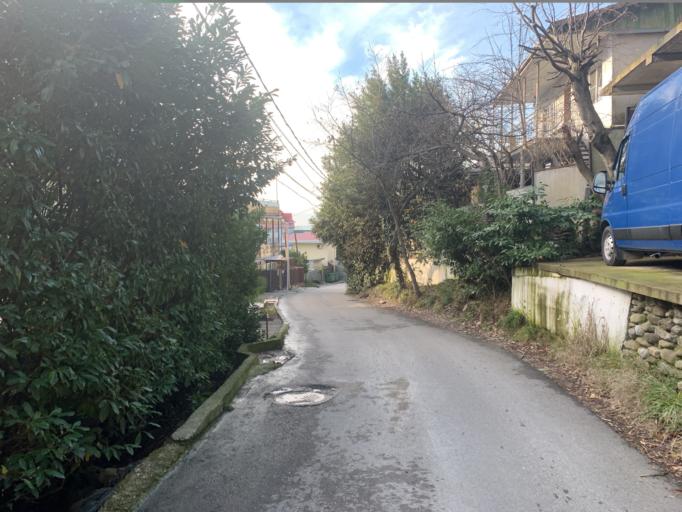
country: RU
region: Krasnodarskiy
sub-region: Sochi City
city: Lazarevskoye
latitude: 43.9216
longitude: 39.3210
